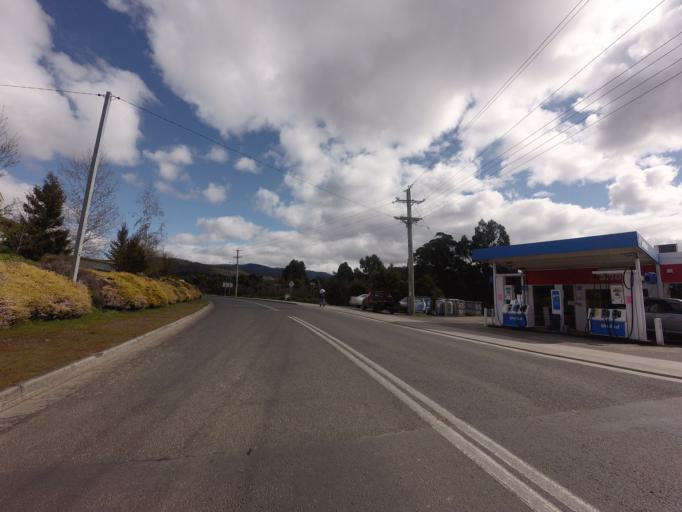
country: AU
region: Tasmania
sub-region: Huon Valley
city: Geeveston
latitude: -43.1649
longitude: 146.9266
